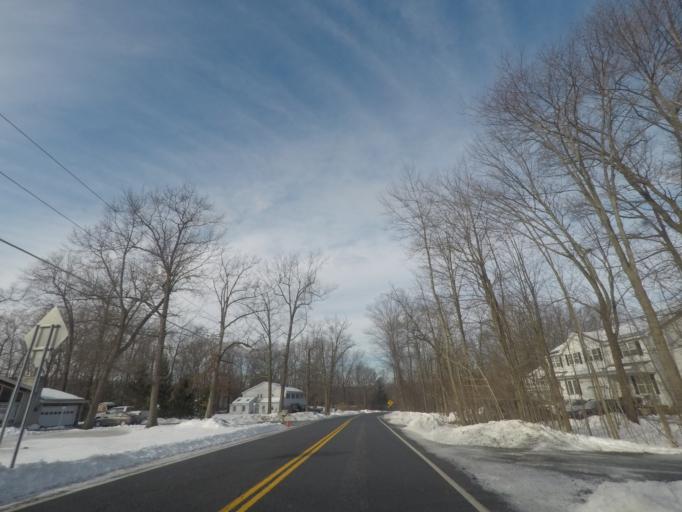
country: US
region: New York
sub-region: Saratoga County
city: Mechanicville
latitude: 42.8538
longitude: -73.7287
